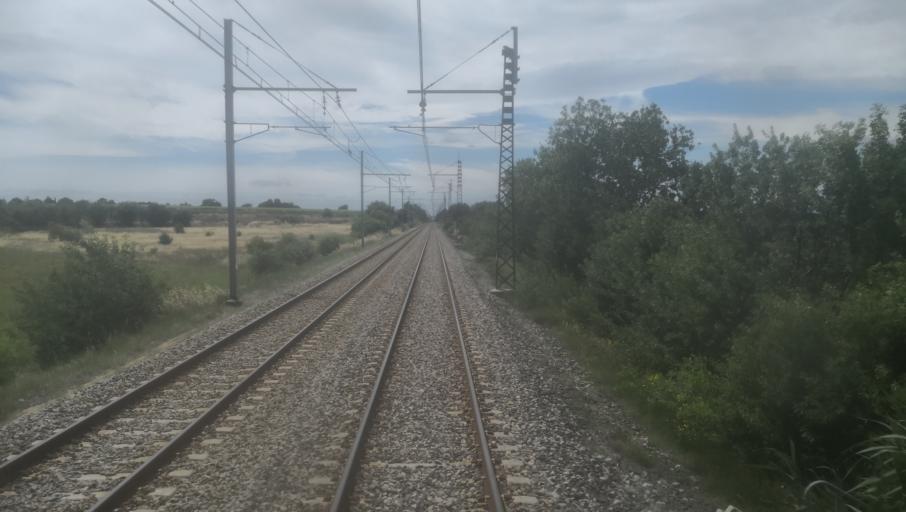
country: FR
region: Languedoc-Roussillon
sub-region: Departement de l'Herault
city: Vias
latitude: 43.3180
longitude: 3.3875
